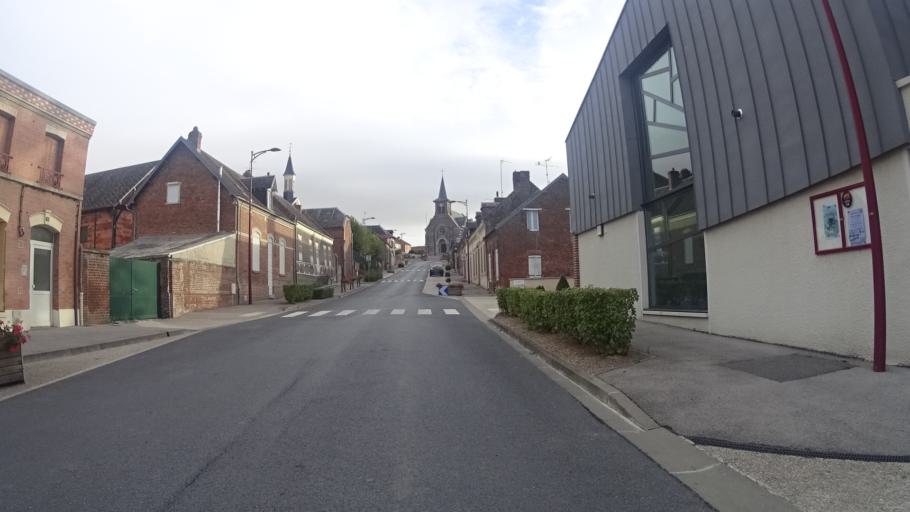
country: FR
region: Picardie
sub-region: Departement de l'Aisne
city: Origny-Sainte-Benoite
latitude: 49.8303
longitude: 3.4680
